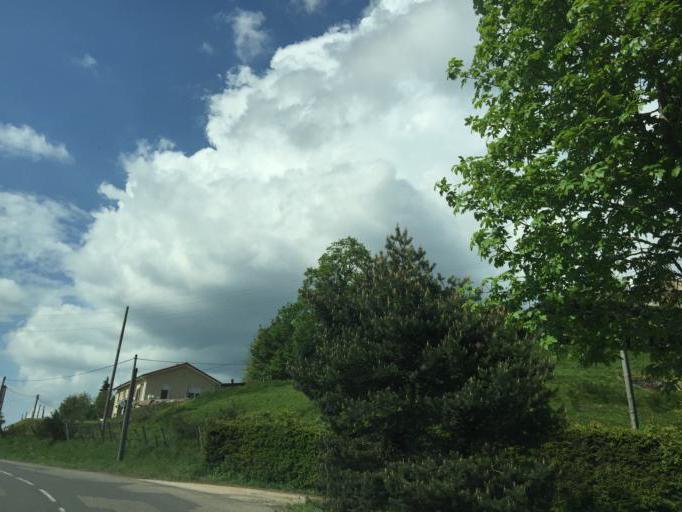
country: FR
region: Rhone-Alpes
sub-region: Departement de la Loire
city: Saint-Genest-Malifaux
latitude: 45.3755
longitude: 4.4911
